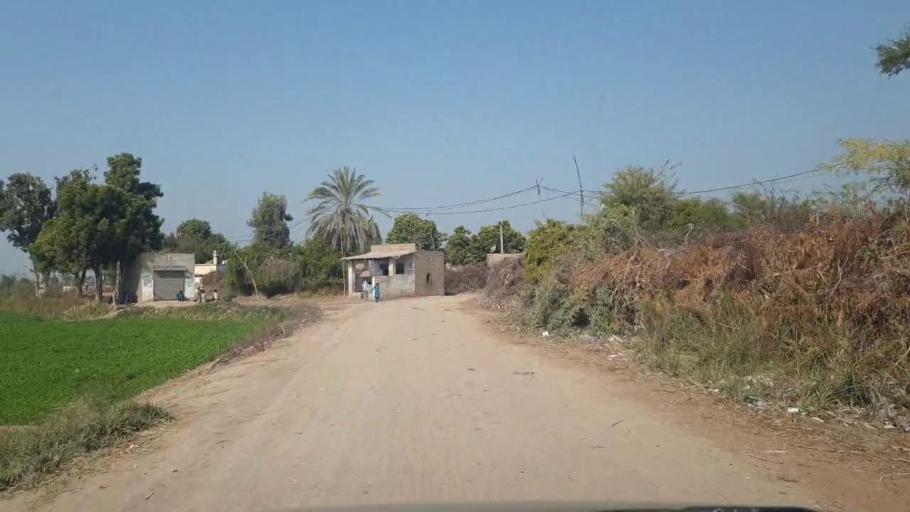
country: PK
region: Sindh
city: Tando Adam
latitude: 25.7900
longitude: 68.6319
